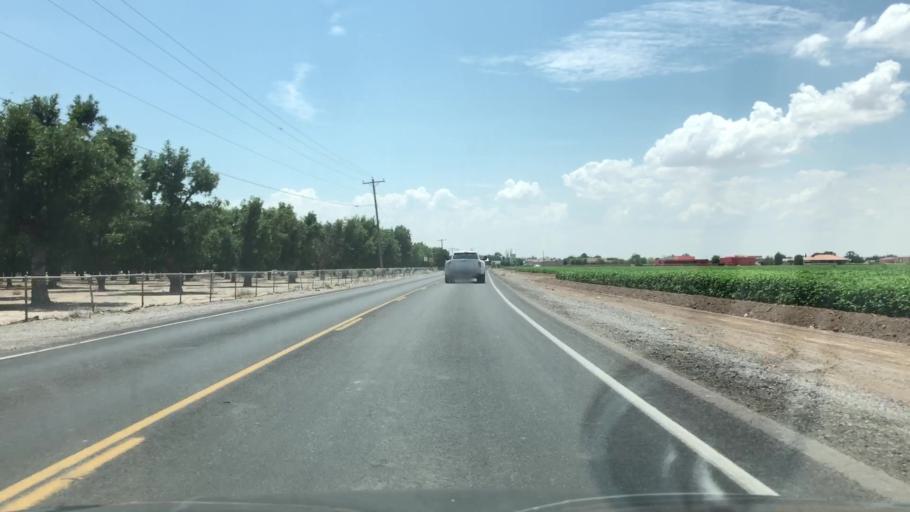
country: US
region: New Mexico
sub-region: Dona Ana County
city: La Union
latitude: 31.9627
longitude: -106.6476
